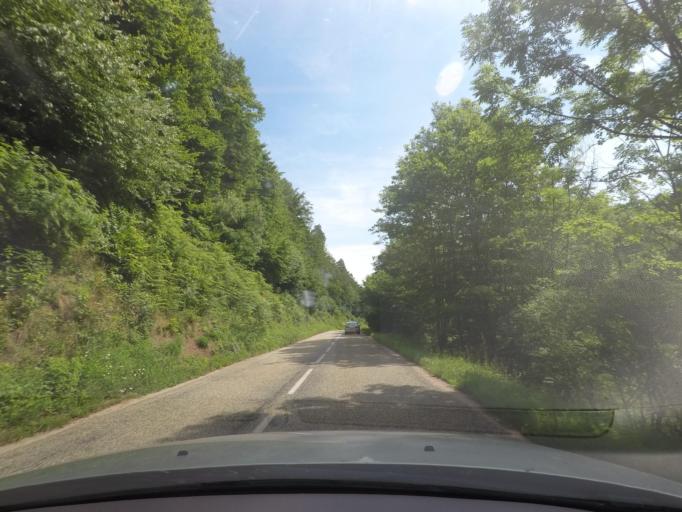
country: FR
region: Lorraine
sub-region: Departement de la Moselle
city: Phalsbourg
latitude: 48.8177
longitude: 7.2500
